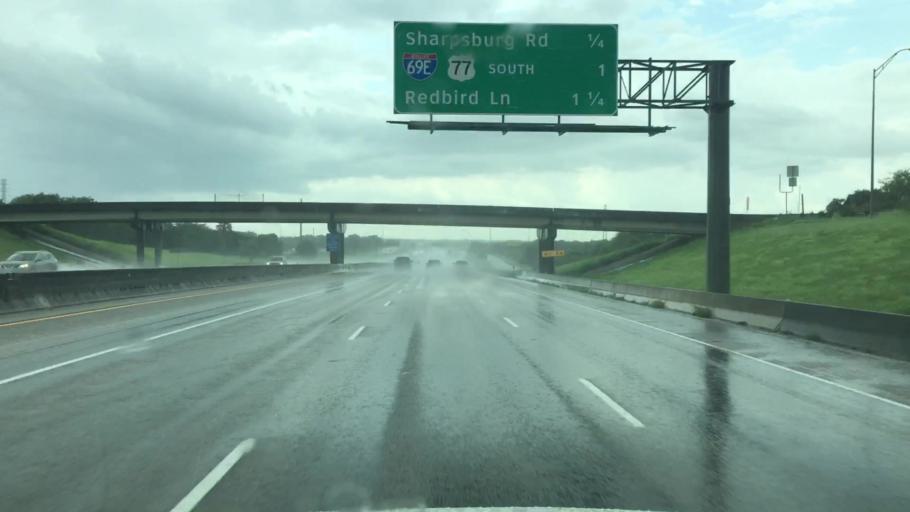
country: US
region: Texas
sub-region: Nueces County
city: Robstown
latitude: 27.8567
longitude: -97.6010
